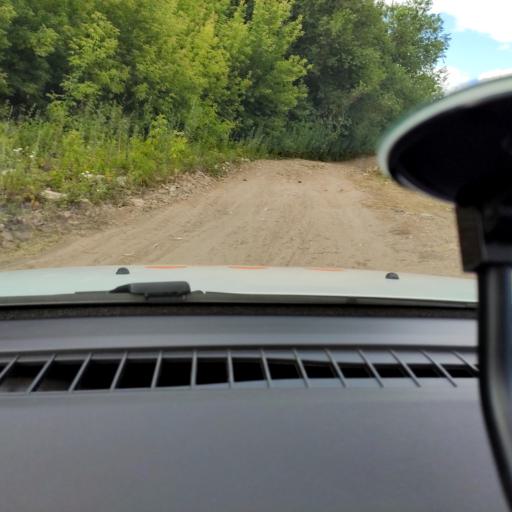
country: RU
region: Samara
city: Samara
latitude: 53.1780
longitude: 50.2158
